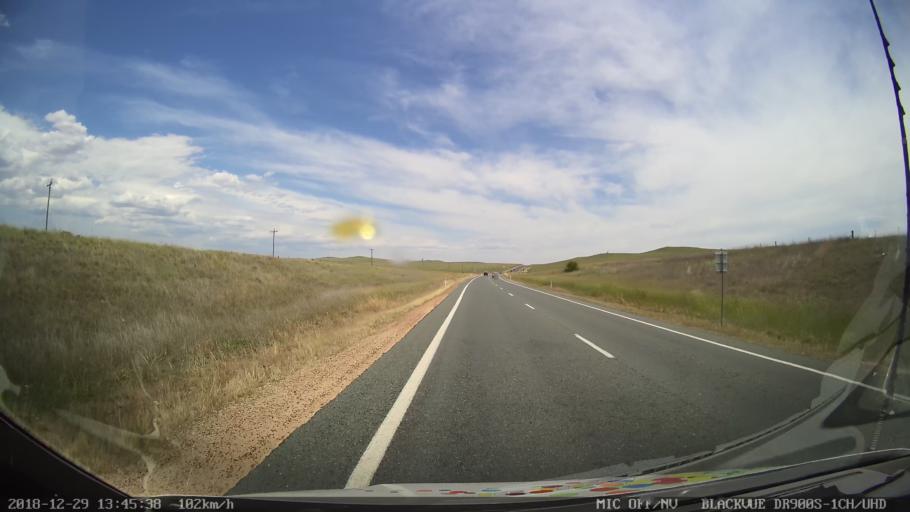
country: AU
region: New South Wales
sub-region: Cooma-Monaro
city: Cooma
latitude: -36.0996
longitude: 149.1452
